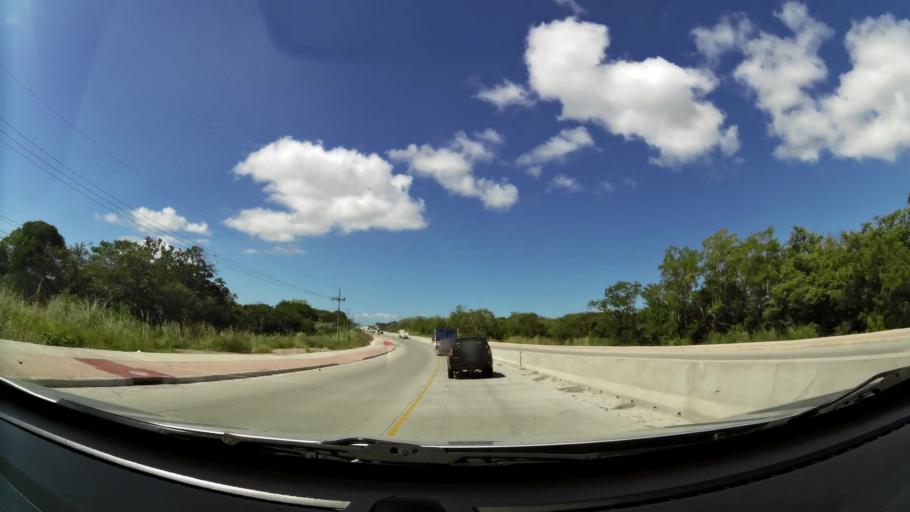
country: CR
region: Guanacaste
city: Bagaces
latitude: 10.5185
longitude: -85.2438
